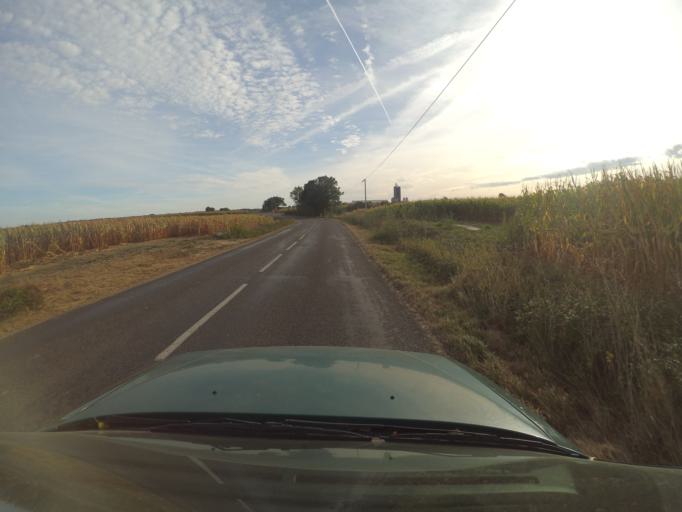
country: FR
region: Pays de la Loire
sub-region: Departement de la Loire-Atlantique
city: Saint-Hilaire-de-Clisson
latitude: 47.0481
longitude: -1.3220
